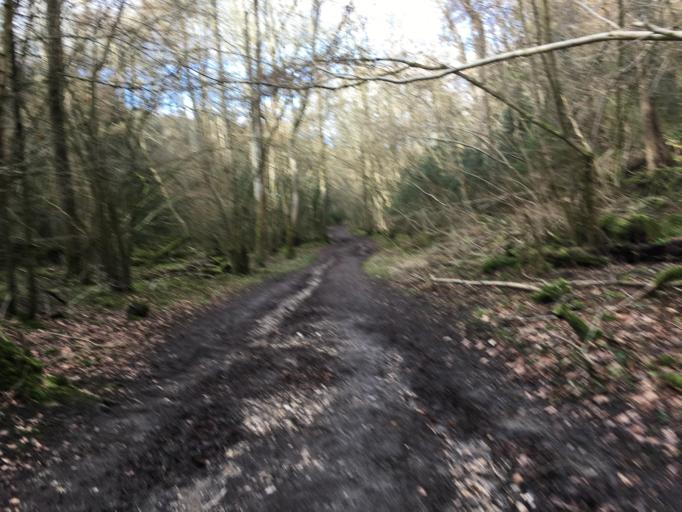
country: GB
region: England
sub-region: Surrey
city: Mickleham
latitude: 51.2525
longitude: -0.3058
